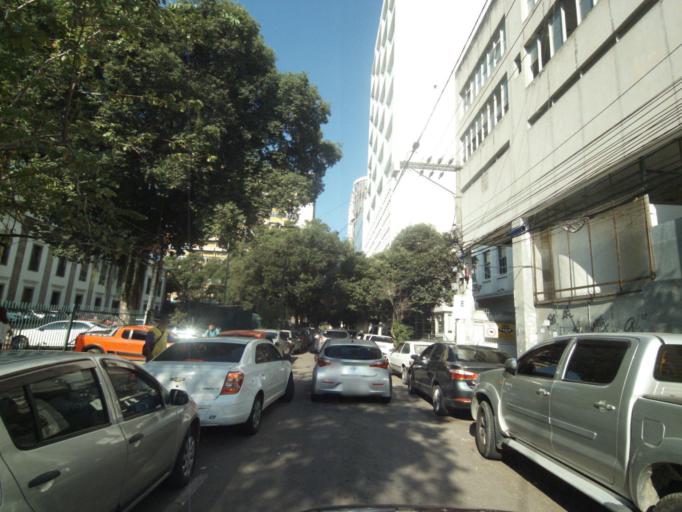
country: BR
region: Rio de Janeiro
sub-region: Niteroi
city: Niteroi
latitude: -22.8920
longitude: -43.1209
